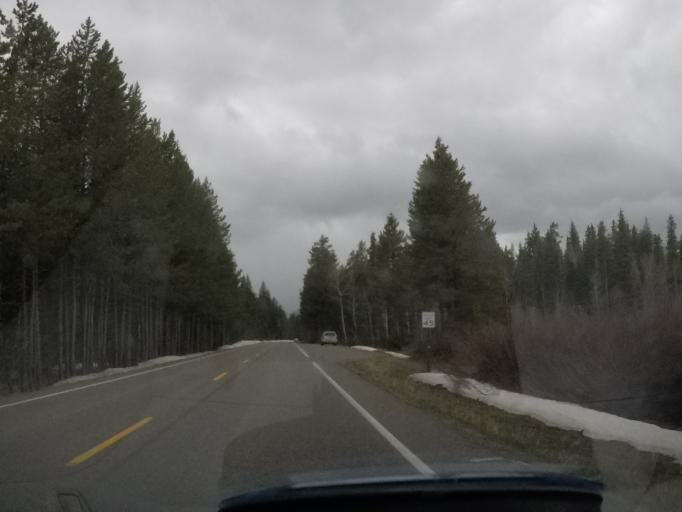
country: US
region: Wyoming
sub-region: Teton County
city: Moose Wilson Road
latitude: 43.9748
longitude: -110.6497
